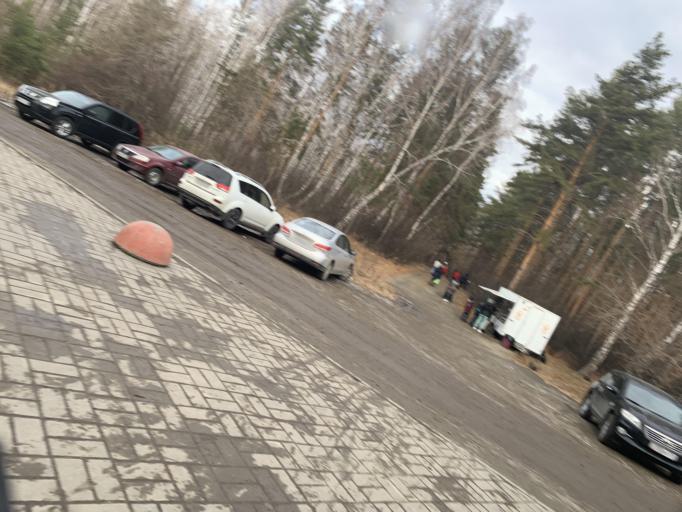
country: RU
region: Chelyabinsk
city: Roshchino
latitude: 55.1968
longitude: 61.2965
